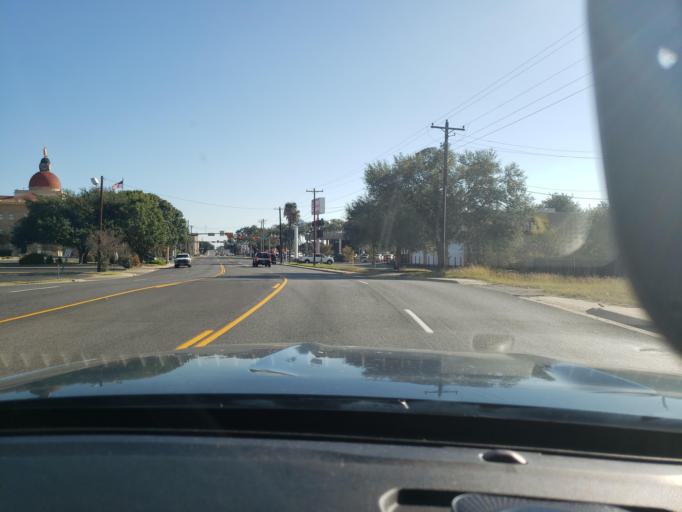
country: US
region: Texas
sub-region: Bee County
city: Beeville
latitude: 28.4003
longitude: -97.7499
